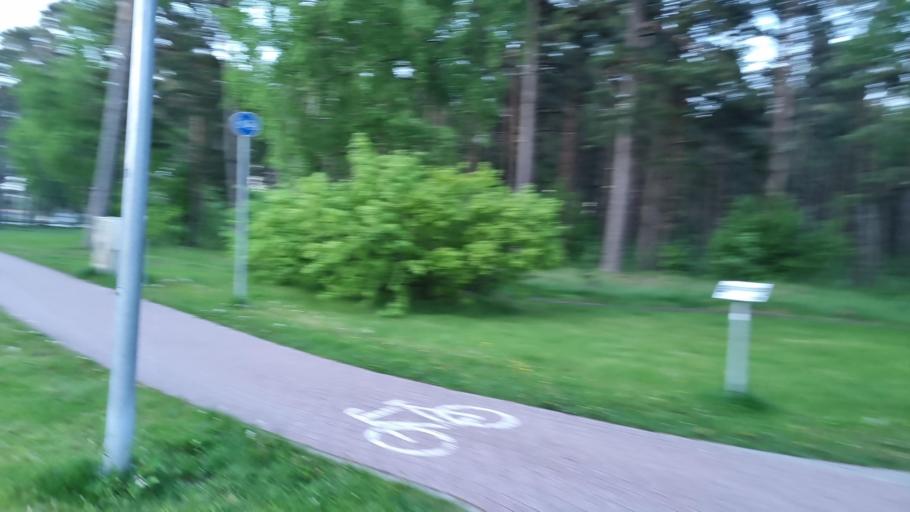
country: LV
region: Ventspils
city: Ventspils
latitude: 57.3837
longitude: 21.5418
